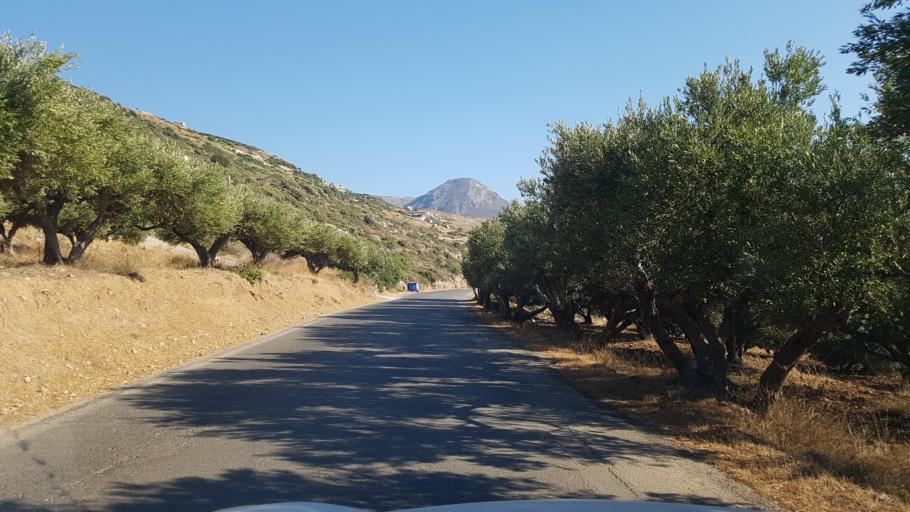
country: GR
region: Crete
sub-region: Nomos Chanias
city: Platanos
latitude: 35.4880
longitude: 23.5886
